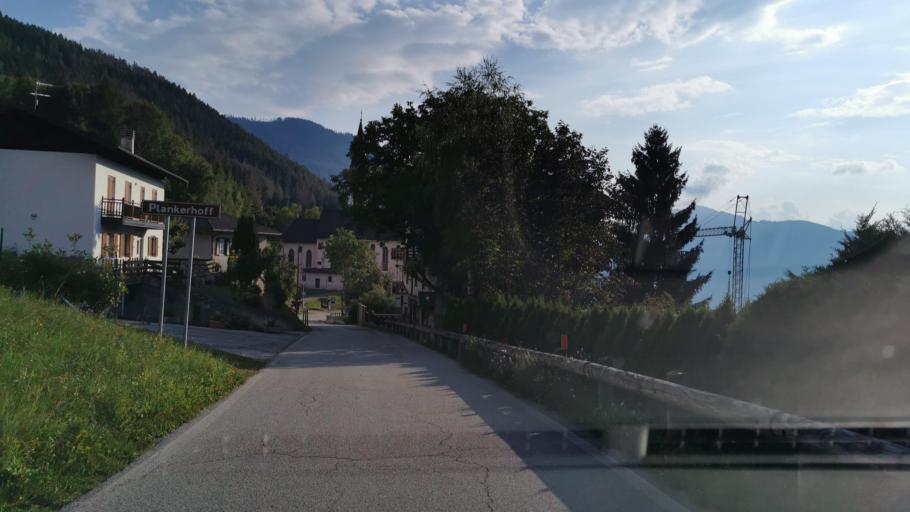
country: IT
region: Trentino-Alto Adige
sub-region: Provincia di Trento
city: Frassilongo
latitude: 46.0906
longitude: 11.2982
